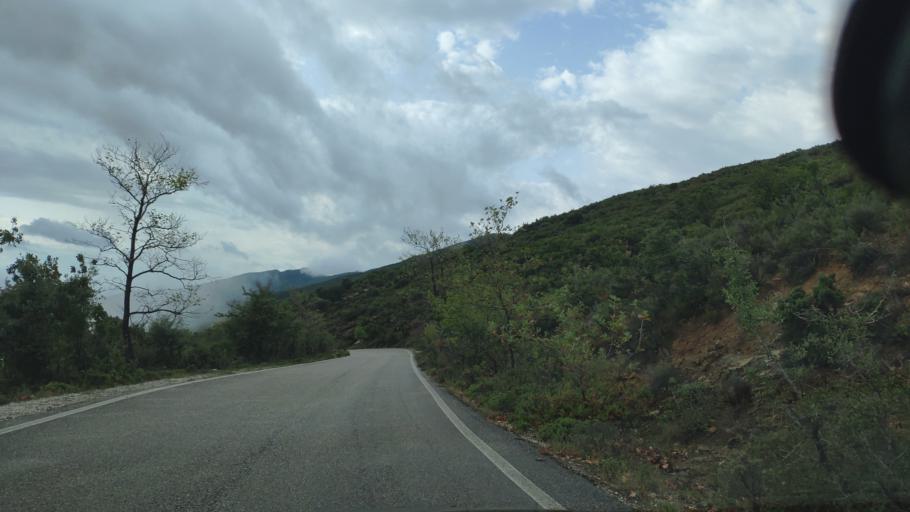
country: GR
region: West Greece
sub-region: Nomos Aitolias kai Akarnanias
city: Sardinia
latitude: 38.8530
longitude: 21.3147
